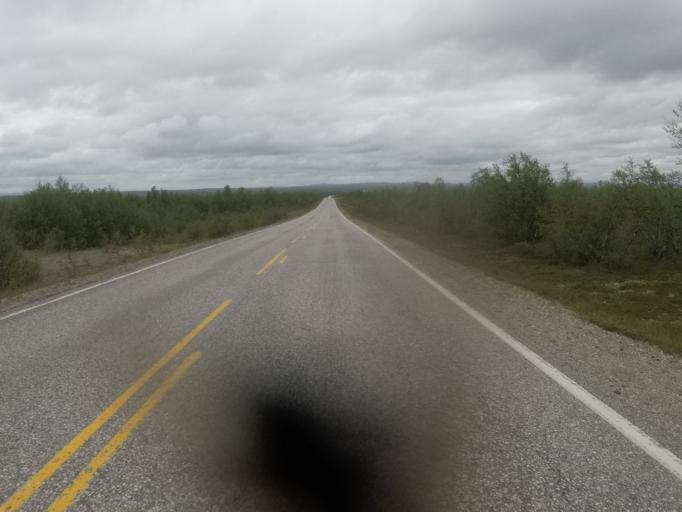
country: NO
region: Finnmark Fylke
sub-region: Kautokeino
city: Kautokeino
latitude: 68.7282
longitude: 23.3081
